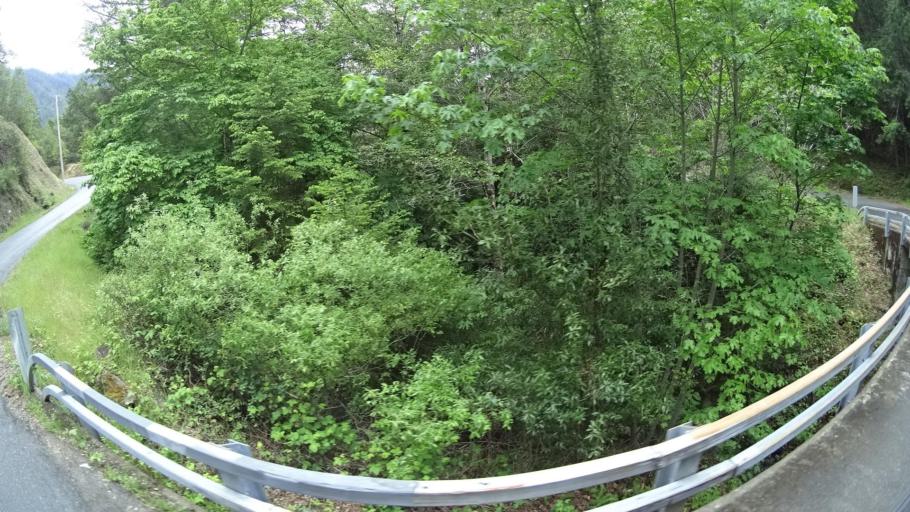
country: US
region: California
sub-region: Humboldt County
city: Willow Creek
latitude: 41.3379
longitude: -123.5200
